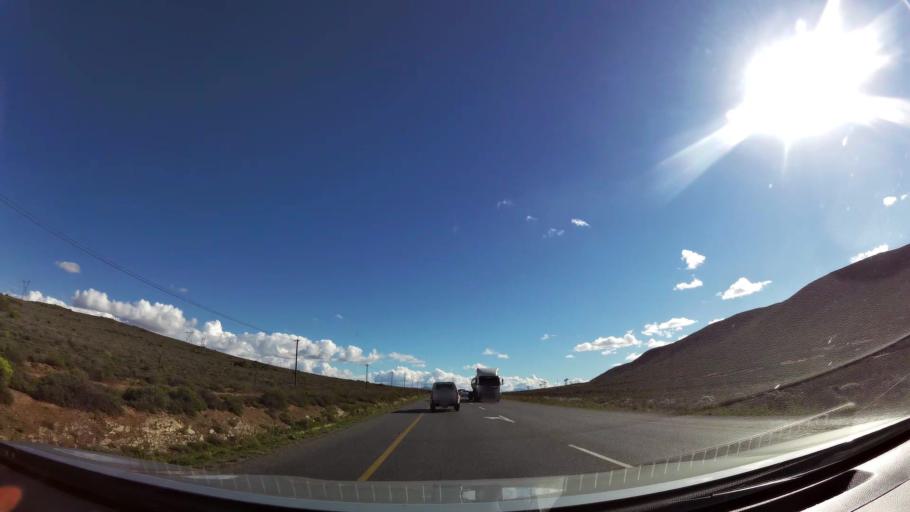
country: ZA
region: Western Cape
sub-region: Cape Winelands District Municipality
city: Worcester
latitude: -33.7348
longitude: 19.6618
